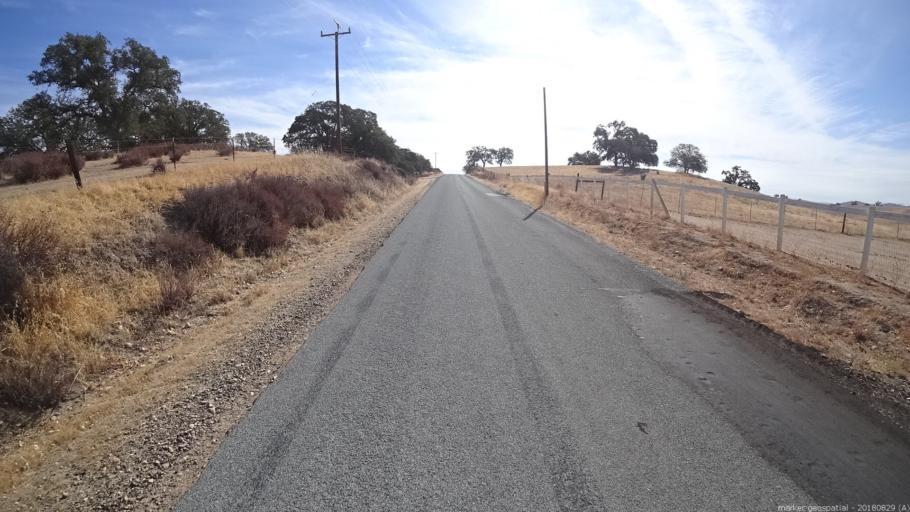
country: US
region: California
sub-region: Monterey County
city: King City
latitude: 35.9663
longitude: -121.1287
